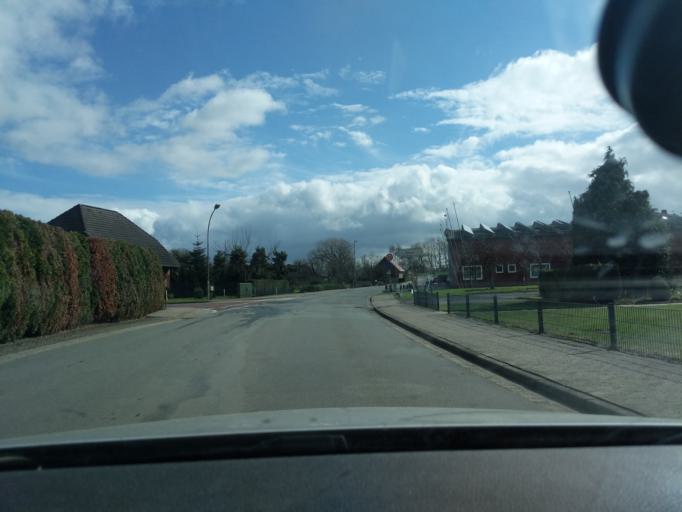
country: DE
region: Lower Saxony
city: Grunendeich
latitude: 53.5686
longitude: 9.6234
